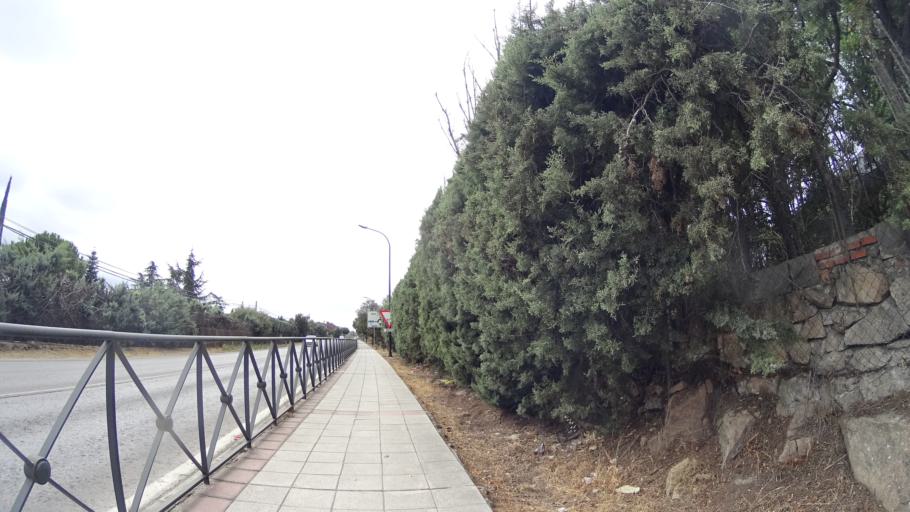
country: ES
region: Madrid
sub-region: Provincia de Madrid
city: Galapagar
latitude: 40.5871
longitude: -4.0120
